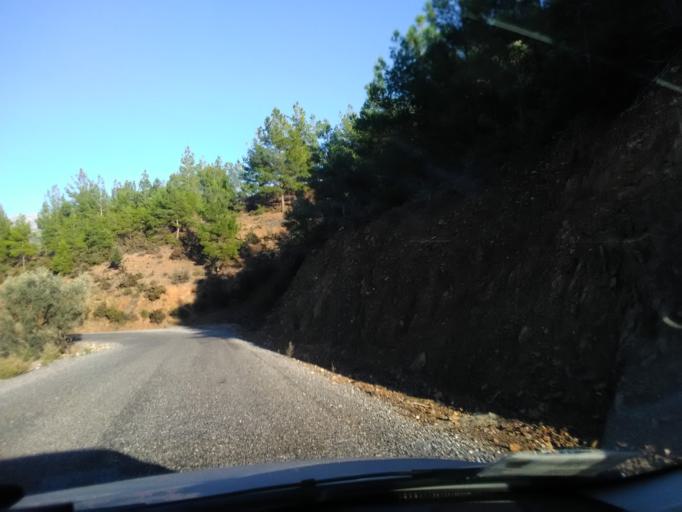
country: TR
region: Antalya
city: Gazipasa
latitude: 36.3064
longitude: 32.4029
